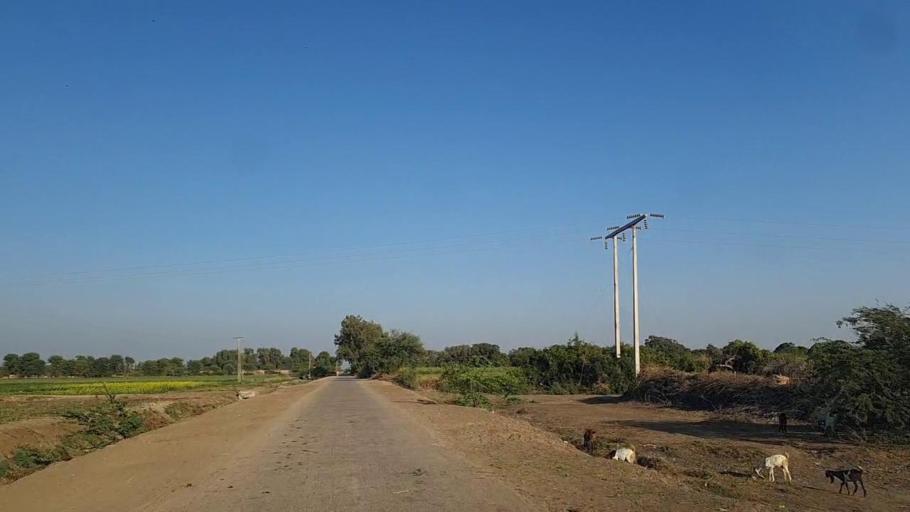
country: PK
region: Sindh
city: Samaro
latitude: 25.3412
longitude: 69.3885
